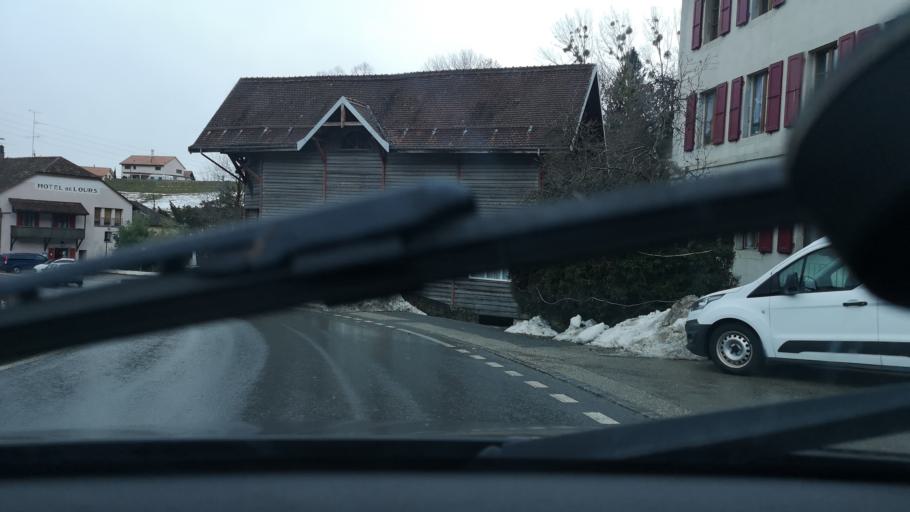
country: CH
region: Vaud
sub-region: Jura-Nord vaudois District
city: Sainte-Croix
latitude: 46.8072
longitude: 6.5468
